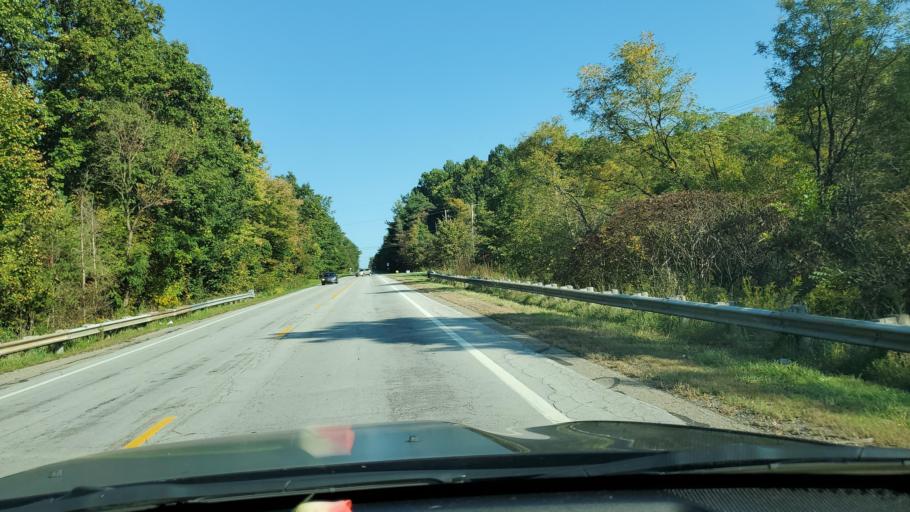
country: US
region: Ohio
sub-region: Trumbull County
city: Brookfield Center
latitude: 41.2759
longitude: -80.5684
